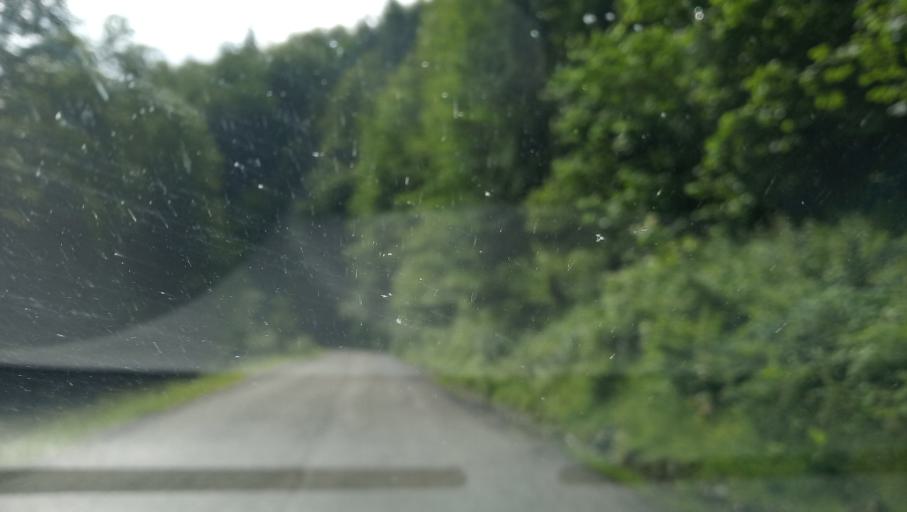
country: RO
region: Hunedoara
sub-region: Oras Petrila
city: Petrila
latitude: 45.4099
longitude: 23.4985
